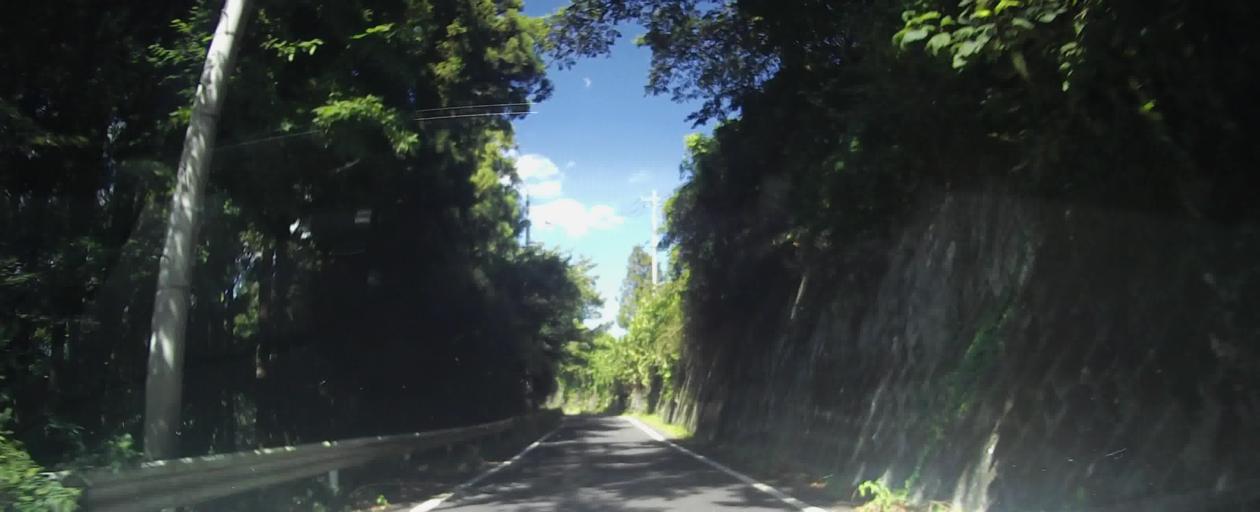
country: JP
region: Gunma
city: Kanekomachi
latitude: 36.4061
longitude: 138.9492
